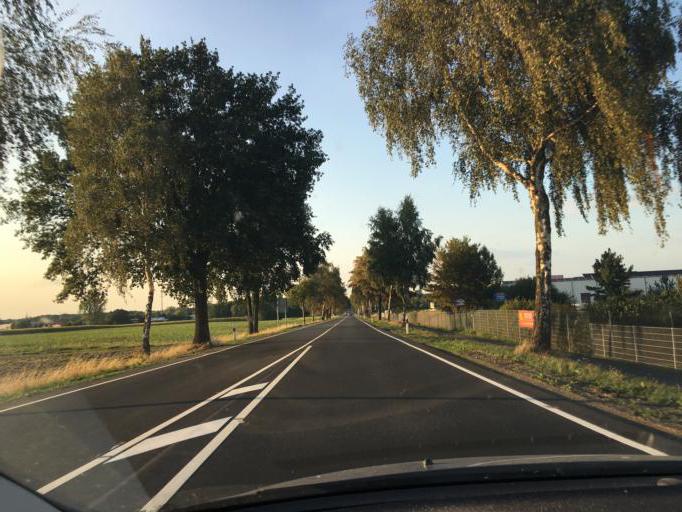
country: DE
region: Lower Saxony
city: Bergen
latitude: 52.7942
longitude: 9.9710
